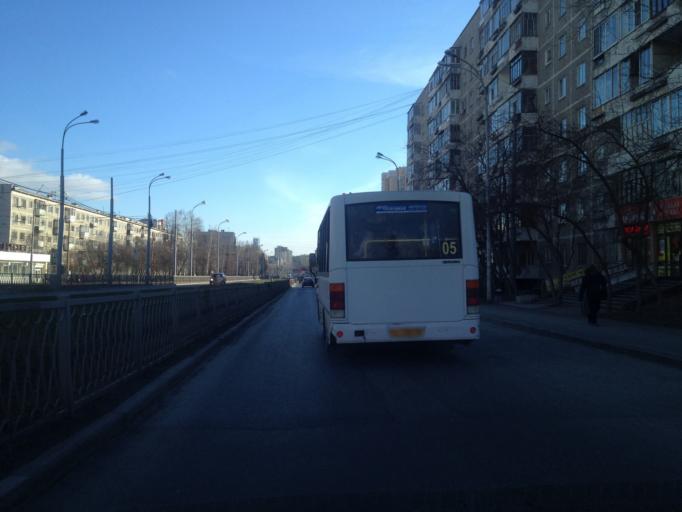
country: RU
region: Sverdlovsk
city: Sovkhoznyy
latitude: 56.8125
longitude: 60.5585
